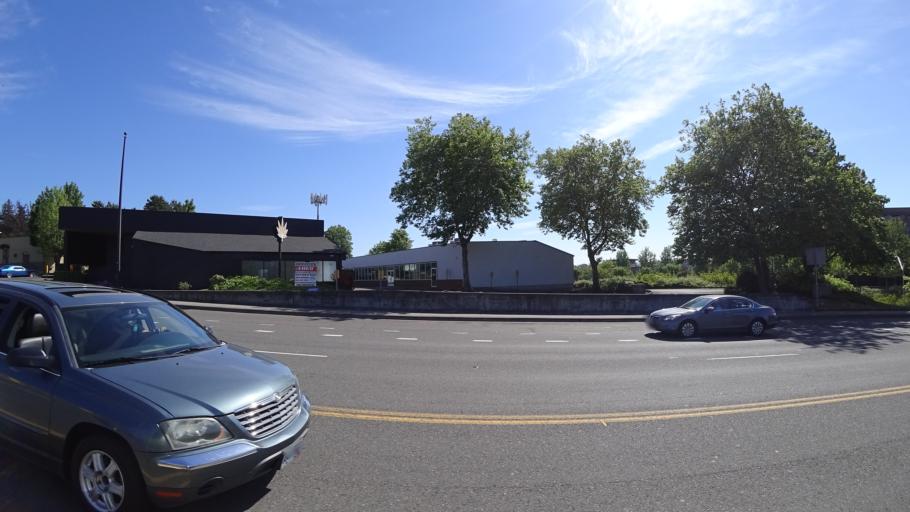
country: US
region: Oregon
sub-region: Washington County
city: Garden Home-Whitford
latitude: 45.4573
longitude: -122.7834
